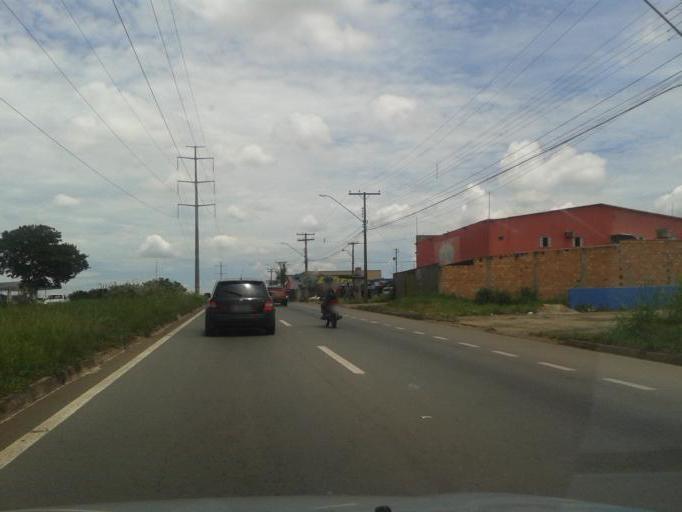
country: BR
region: Goias
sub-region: Aparecida De Goiania
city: Aparecida de Goiania
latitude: -16.7773
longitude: -49.2960
